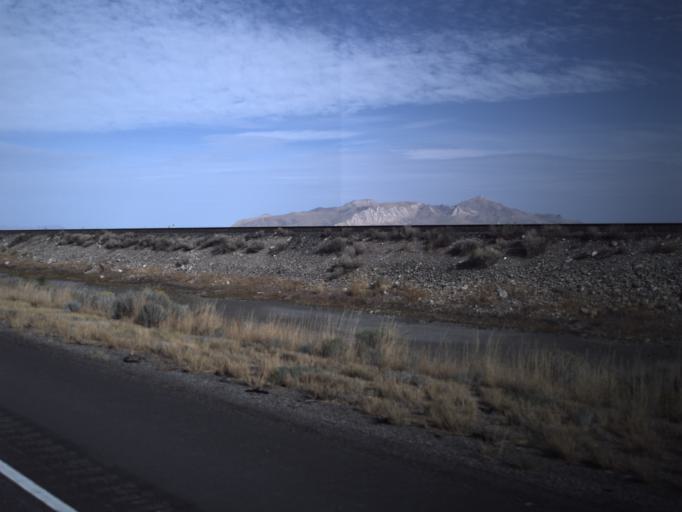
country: US
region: Utah
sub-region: Tooele County
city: Grantsville
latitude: 40.6767
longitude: -112.4046
